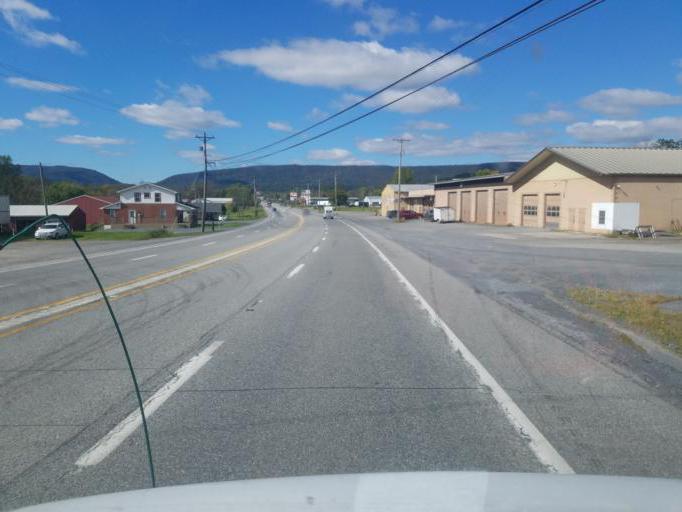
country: US
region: Pennsylvania
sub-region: Bedford County
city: Earlston
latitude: 40.0197
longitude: -78.3330
